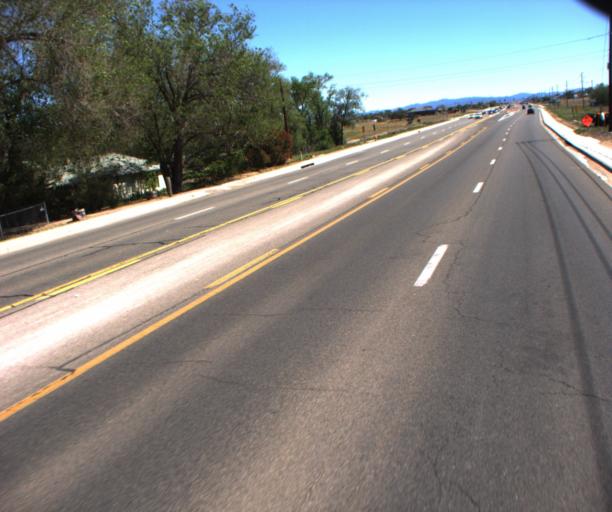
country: US
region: Arizona
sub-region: Yavapai County
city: Chino Valley
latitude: 34.7430
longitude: -112.4546
